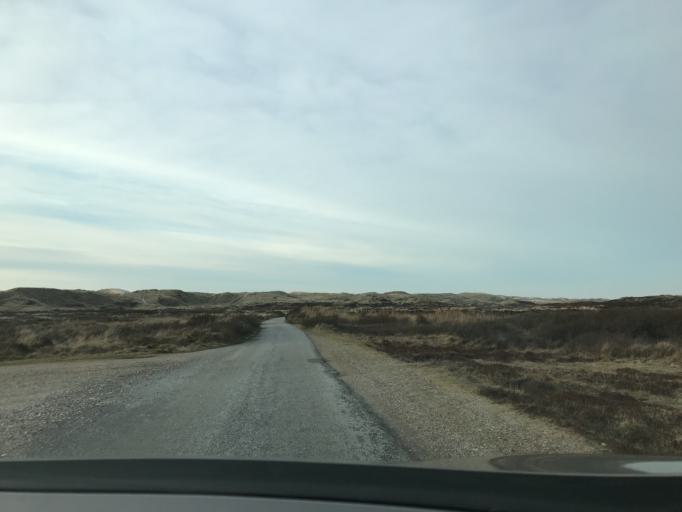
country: DK
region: Central Jutland
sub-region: Ringkobing-Skjern Kommune
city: Hvide Sande
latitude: 55.8083
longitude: 8.1807
